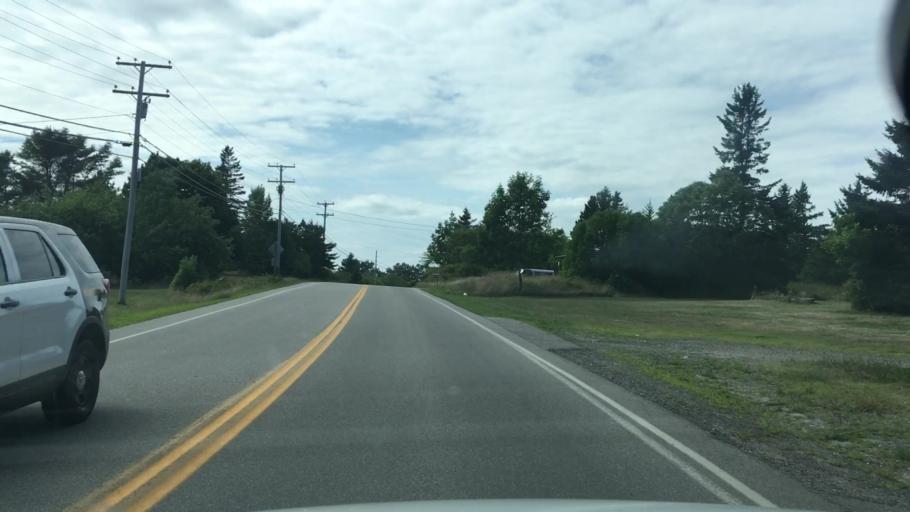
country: US
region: Maine
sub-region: Washington County
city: Eastport
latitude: 44.9127
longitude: -67.0014
